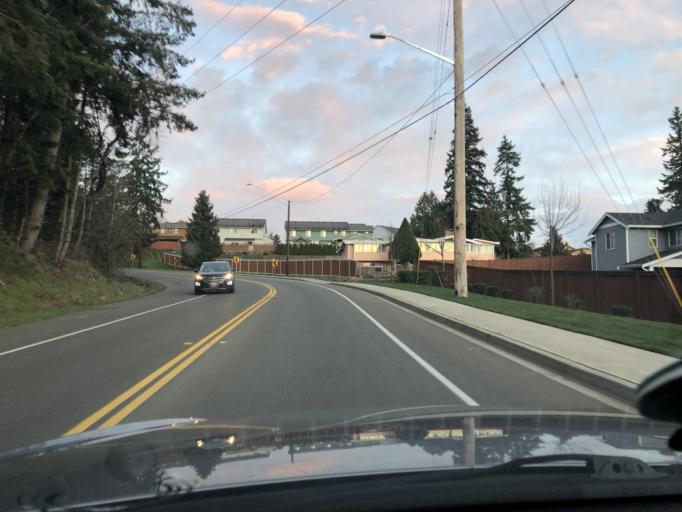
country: US
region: Washington
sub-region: King County
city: Lakeland North
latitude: 47.3145
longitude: -122.2725
